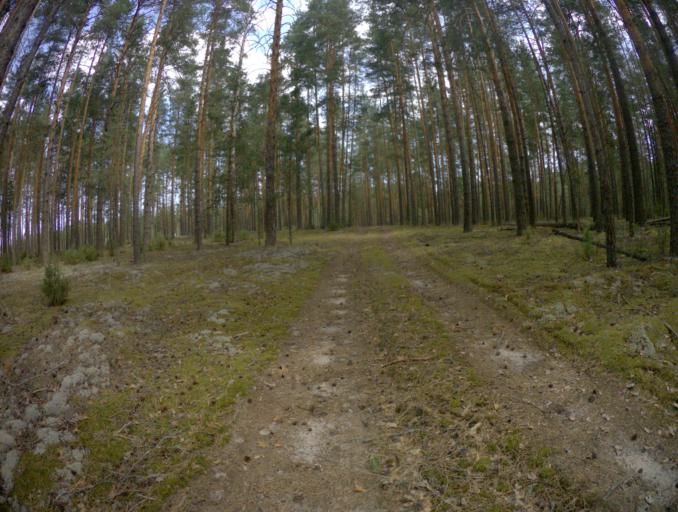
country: RU
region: Ivanovo
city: Talitsy
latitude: 56.3814
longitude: 42.3174
